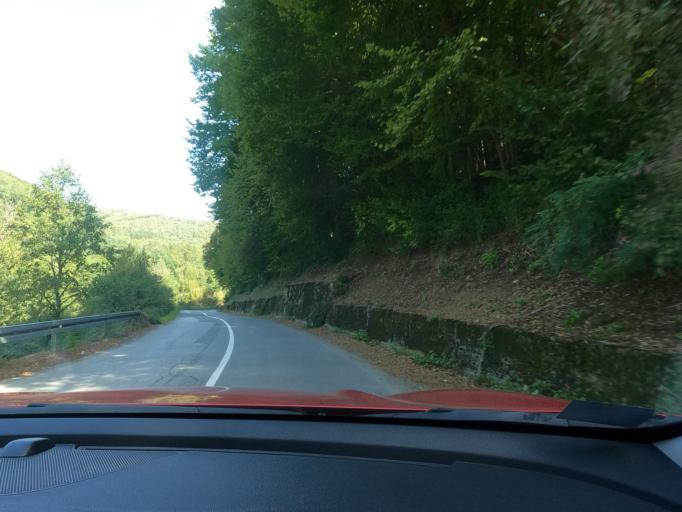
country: HR
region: Sisacko-Moslavacka
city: Petrinja
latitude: 45.3739
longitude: 16.2822
